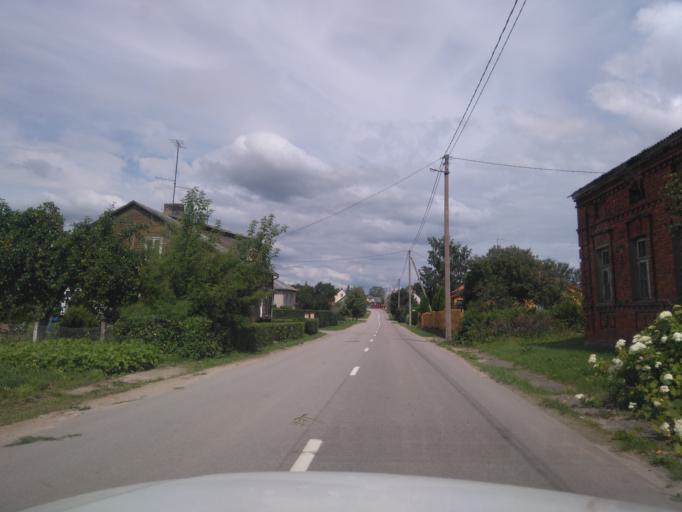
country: LT
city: Virbalis
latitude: 54.6273
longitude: 22.8232
